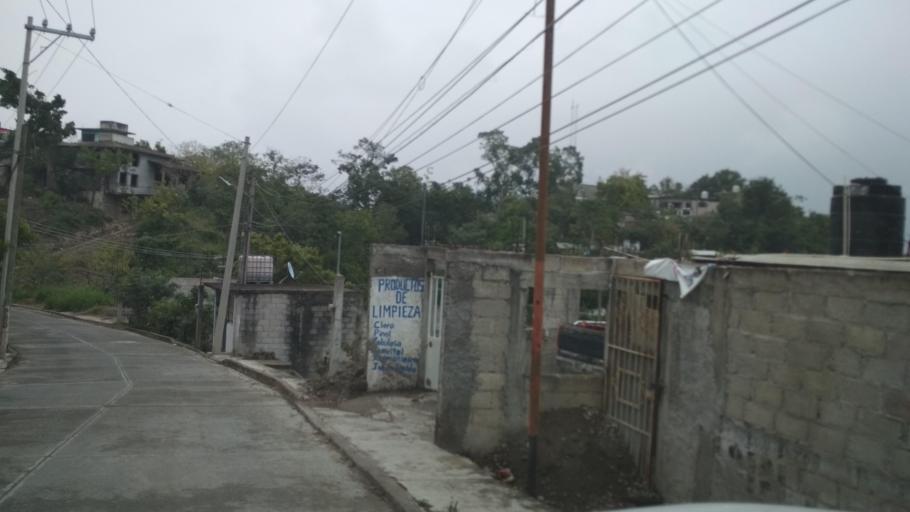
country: MX
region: Veracruz
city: Papantla de Olarte
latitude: 20.4432
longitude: -97.3116
